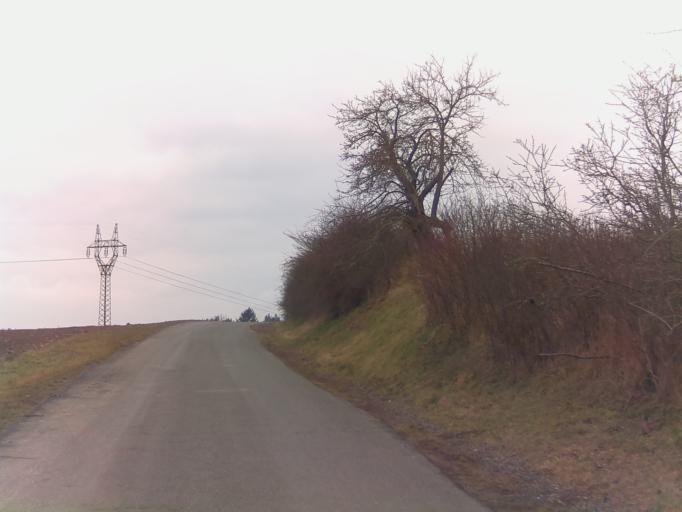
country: DE
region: Thuringia
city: Bad Blankenburg
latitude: 50.6997
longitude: 11.2431
